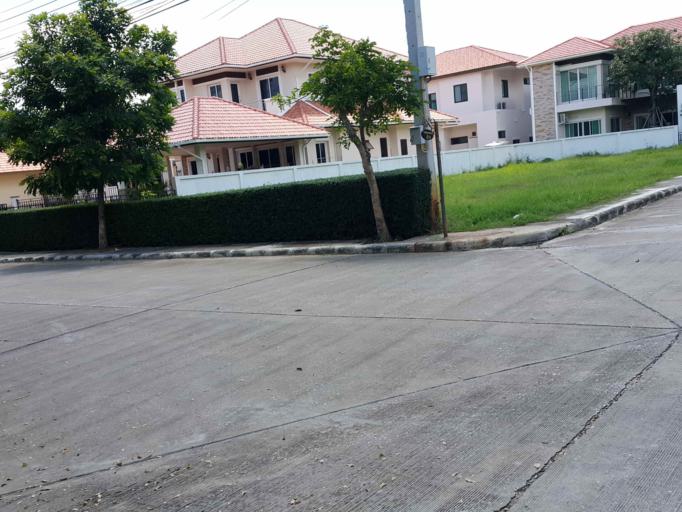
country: TH
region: Chiang Mai
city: Saraphi
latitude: 18.7553
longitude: 99.0413
